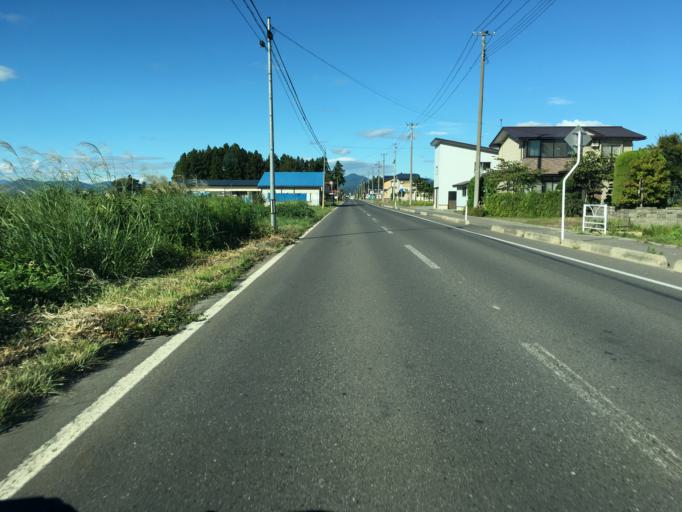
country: JP
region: Yamagata
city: Takahata
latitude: 37.9659
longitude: 140.1570
